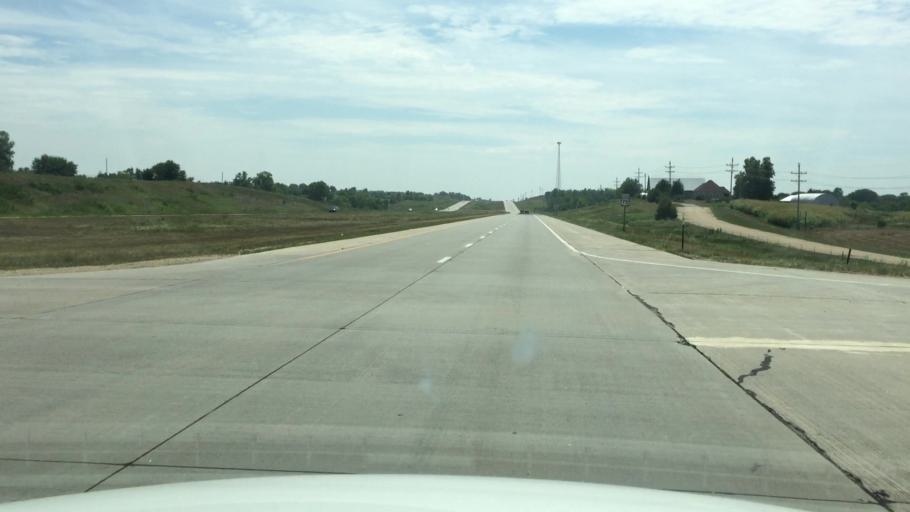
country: US
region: Kansas
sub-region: Jackson County
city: Holton
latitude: 39.2598
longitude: -95.7201
